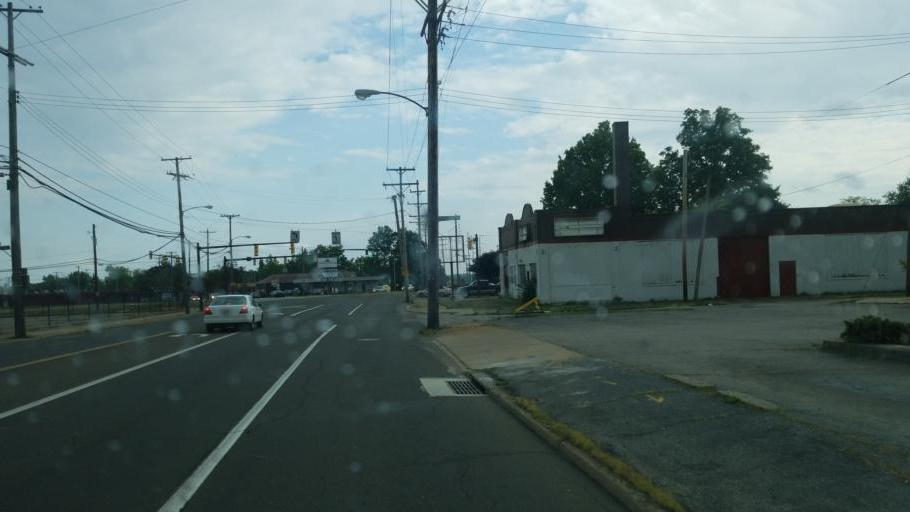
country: US
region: Ohio
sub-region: Mahoning County
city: Youngstown
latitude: 41.1254
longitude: -80.6642
